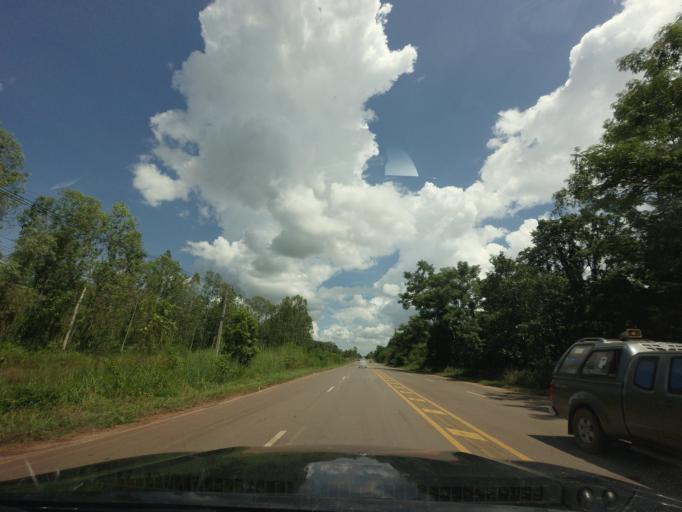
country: TH
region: Changwat Udon Thani
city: Ban Dung
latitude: 17.6826
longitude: 103.2207
